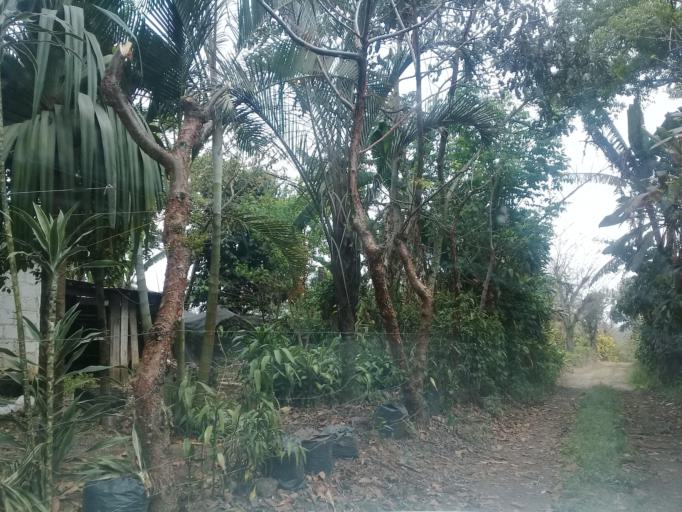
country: MX
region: Veracruz
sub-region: Cordoba
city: Fredepo
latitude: 18.8618
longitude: -96.9919
